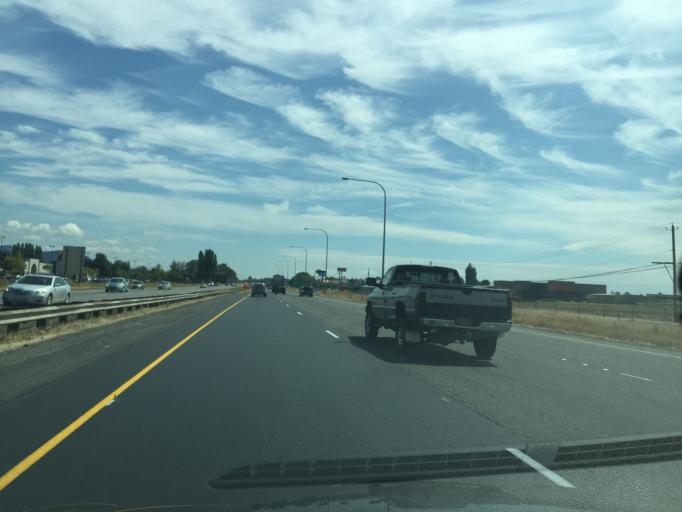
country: US
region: Washington
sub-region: Skagit County
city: Burlington
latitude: 48.4650
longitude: -122.3417
